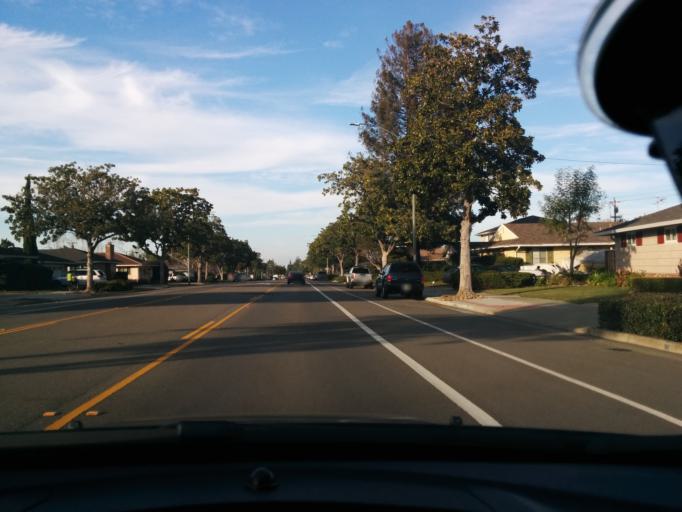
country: US
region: California
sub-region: Santa Clara County
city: Cupertino
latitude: 37.3423
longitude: -122.0500
